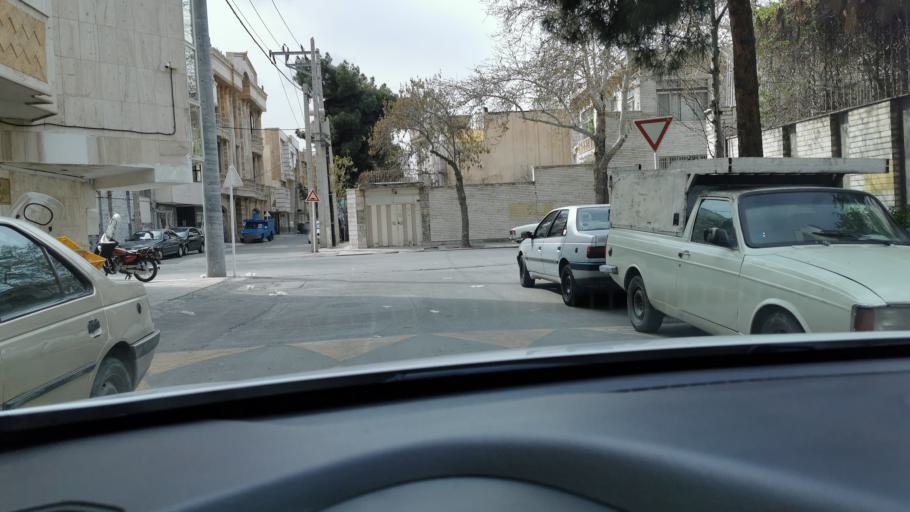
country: IR
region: Razavi Khorasan
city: Mashhad
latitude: 36.2918
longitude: 59.5749
